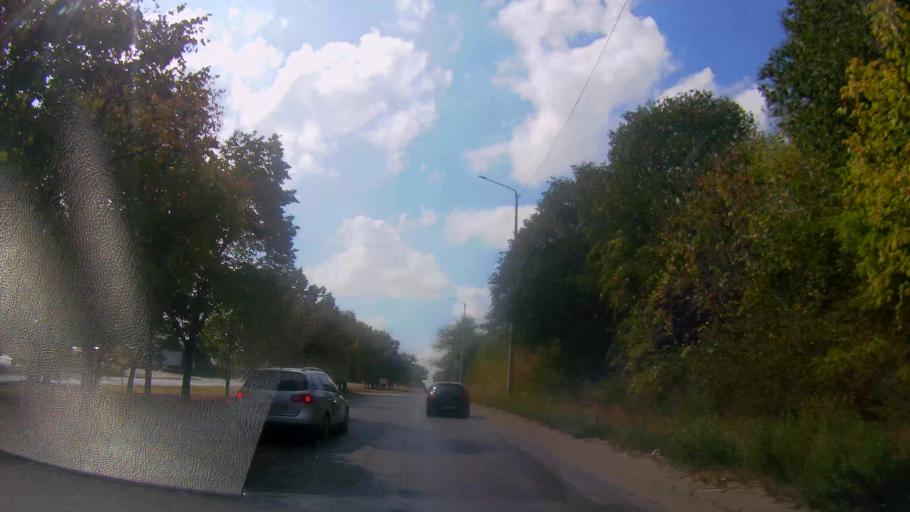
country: BG
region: Ruse
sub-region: Obshtina Ruse
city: Ruse
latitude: 43.8723
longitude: 26.0157
